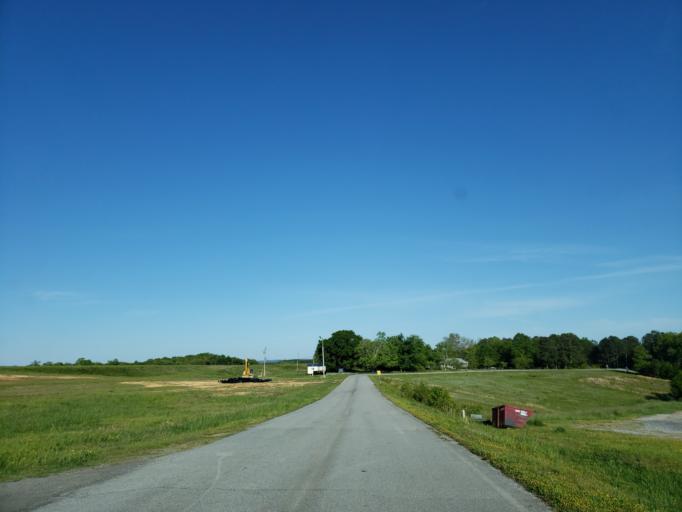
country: US
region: Georgia
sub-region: Polk County
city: Aragon
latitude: 34.0177
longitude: -85.1490
